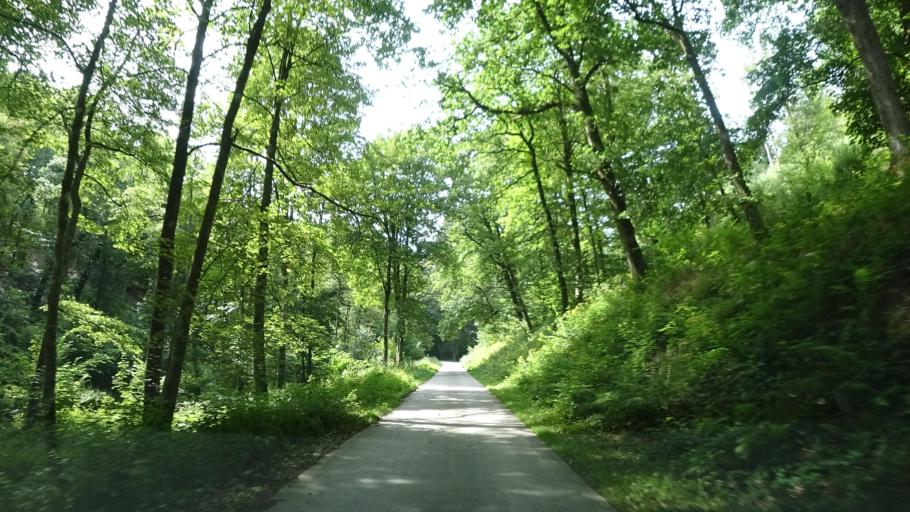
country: BE
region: Wallonia
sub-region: Province du Luxembourg
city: Herbeumont
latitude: 49.7729
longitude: 5.2558
